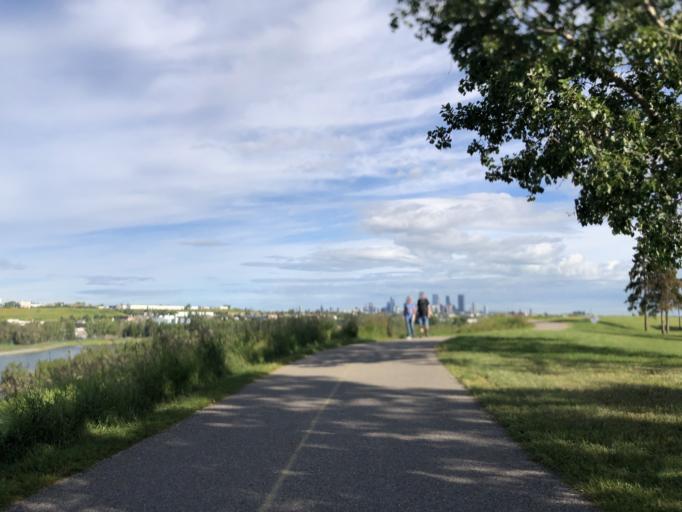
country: CA
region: Alberta
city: Calgary
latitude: 50.9943
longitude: -114.0227
